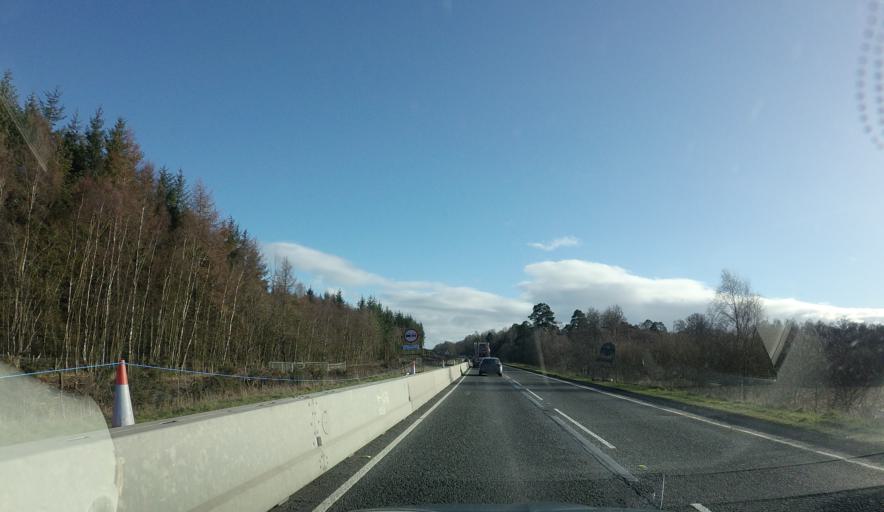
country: GB
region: Scotland
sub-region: Perth and Kinross
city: Bankfoot
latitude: 56.5184
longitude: -3.5169
